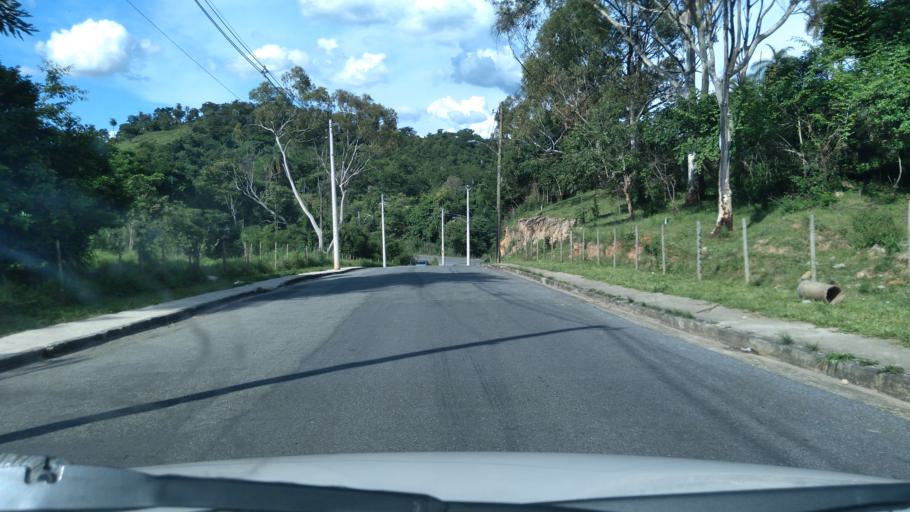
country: BR
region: Minas Gerais
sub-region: Belo Horizonte
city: Belo Horizonte
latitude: -19.8559
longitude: -43.8768
